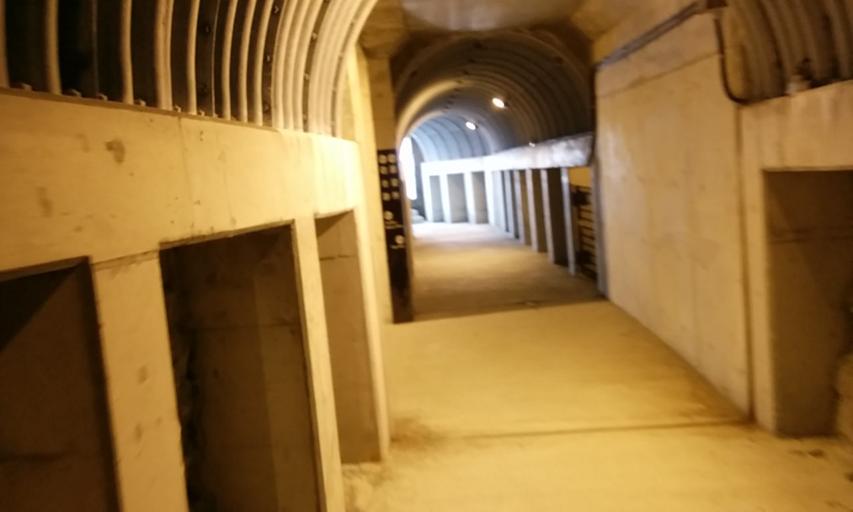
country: JP
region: Oita
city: Tsukumiura
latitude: 33.3381
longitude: 132.0301
